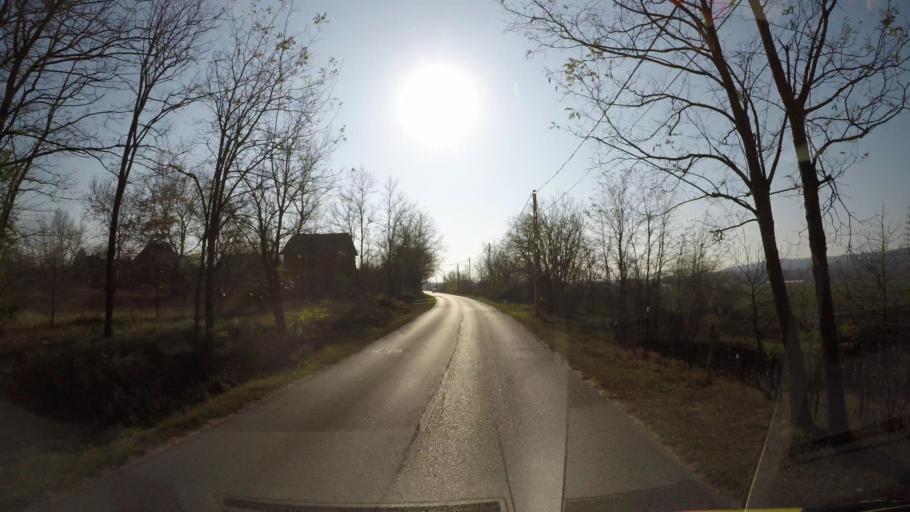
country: HU
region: Pest
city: Leanyfalu
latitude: 47.6995
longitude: 19.1044
